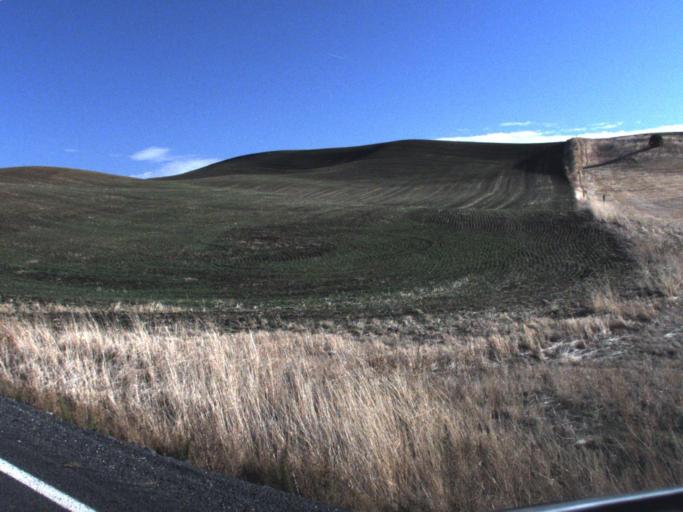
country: US
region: Washington
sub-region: Whitman County
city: Pullman
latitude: 46.7122
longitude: -117.2643
